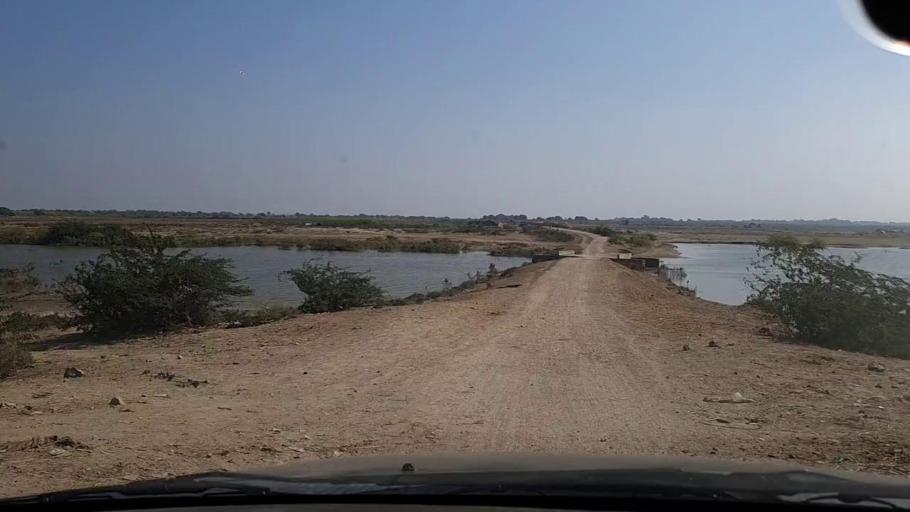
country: PK
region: Sindh
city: Chuhar Jamali
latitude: 24.4219
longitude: 67.8223
